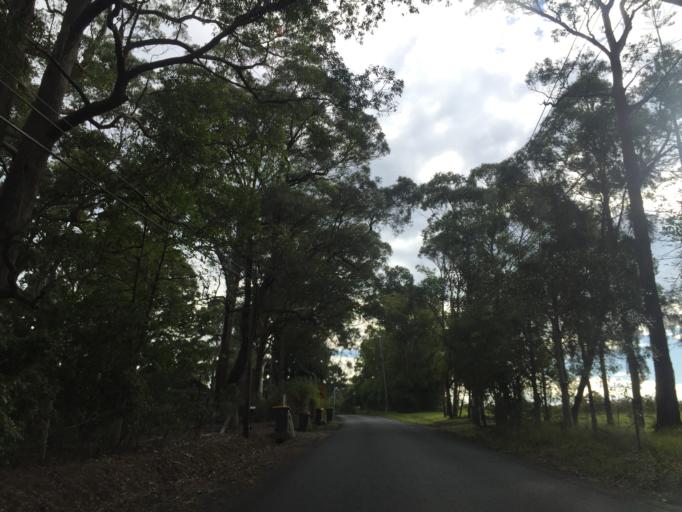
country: AU
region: New South Wales
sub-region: Hornsby Shire
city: Galston
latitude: -33.6493
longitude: 151.0627
